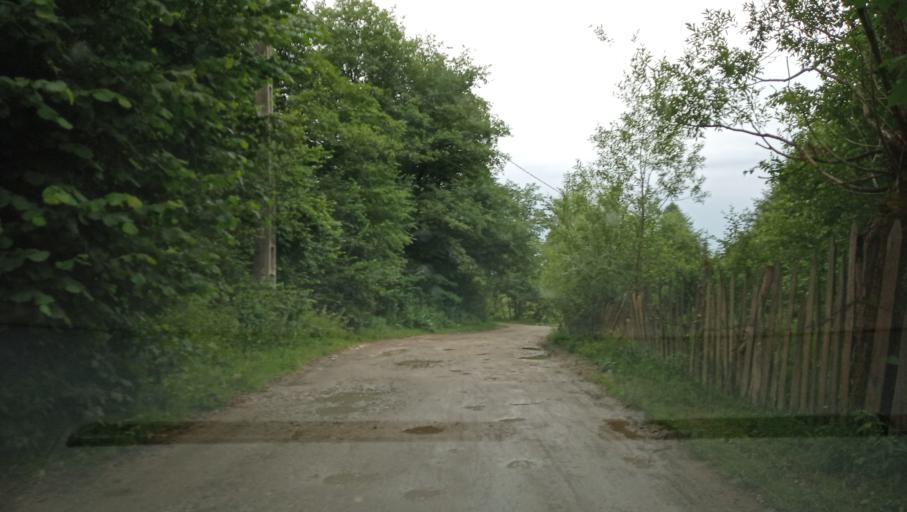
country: RO
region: Hunedoara
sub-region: Oras Petrila
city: Petrila
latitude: 45.4682
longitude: 23.4199
